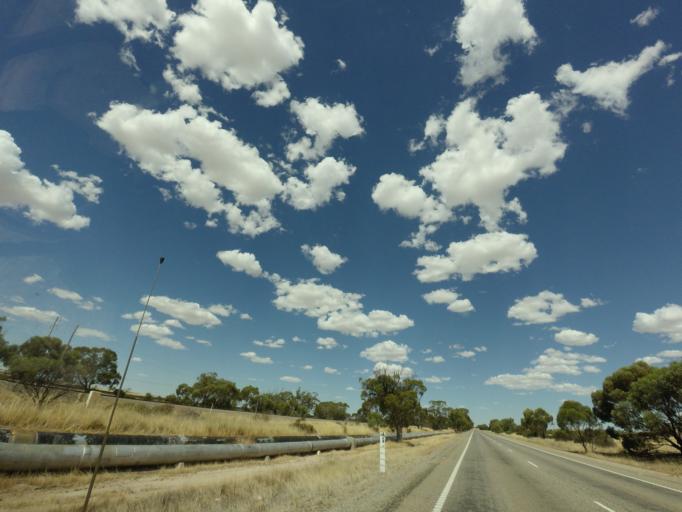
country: AU
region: Western Australia
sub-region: Cunderdin
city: Cunderdin
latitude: -31.6340
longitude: 117.1537
